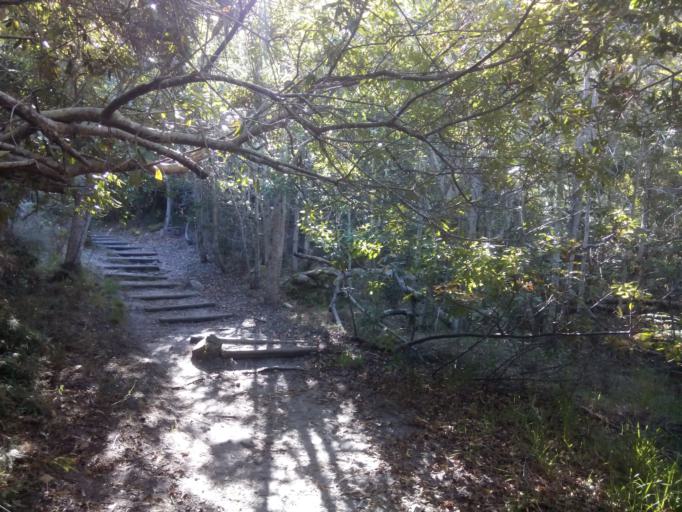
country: ZA
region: Western Cape
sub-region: City of Cape Town
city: Newlands
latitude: -33.9878
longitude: 18.4282
